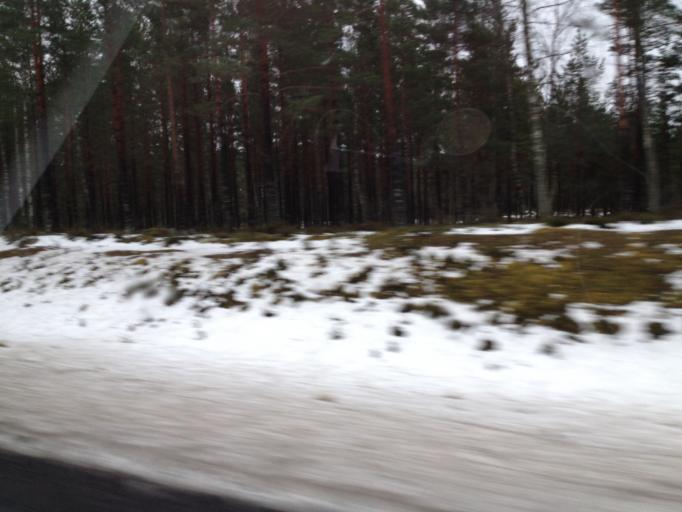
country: FI
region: Uusimaa
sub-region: Raaseporin
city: Ekenaes
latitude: 59.9066
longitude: 23.2172
